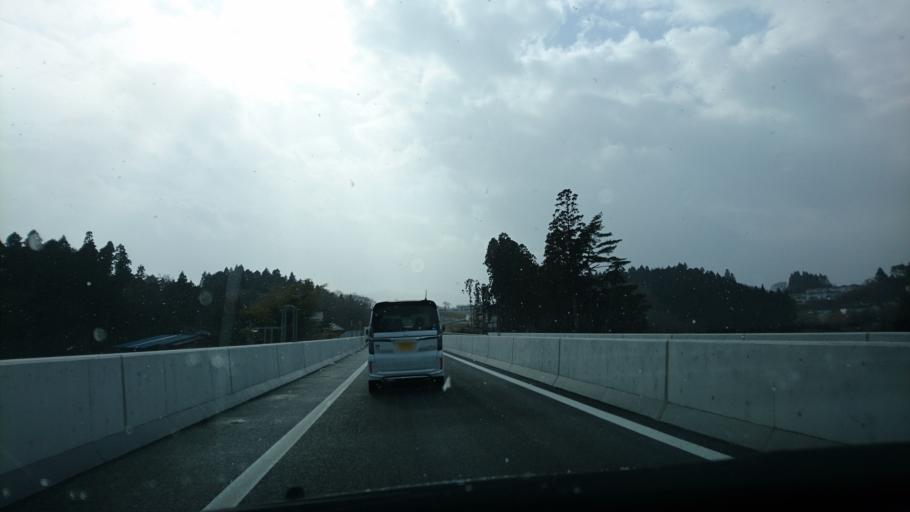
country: JP
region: Iwate
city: Ofunato
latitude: 38.7955
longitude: 141.5256
